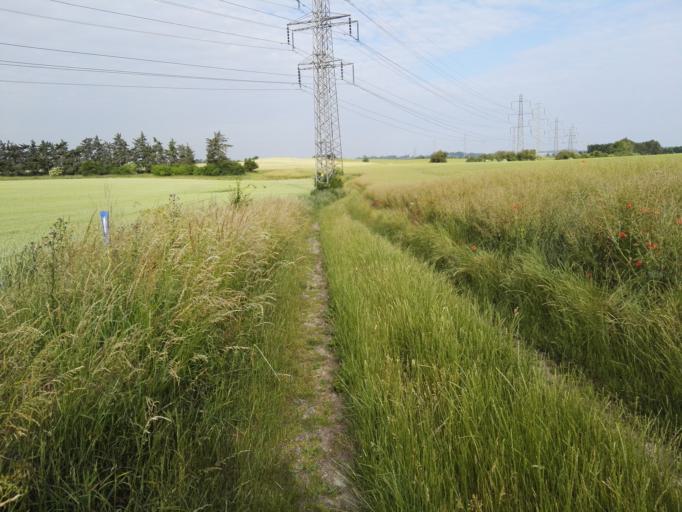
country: DK
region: Zealand
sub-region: Roskilde Kommune
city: Jyllinge
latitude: 55.7867
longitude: 12.0901
